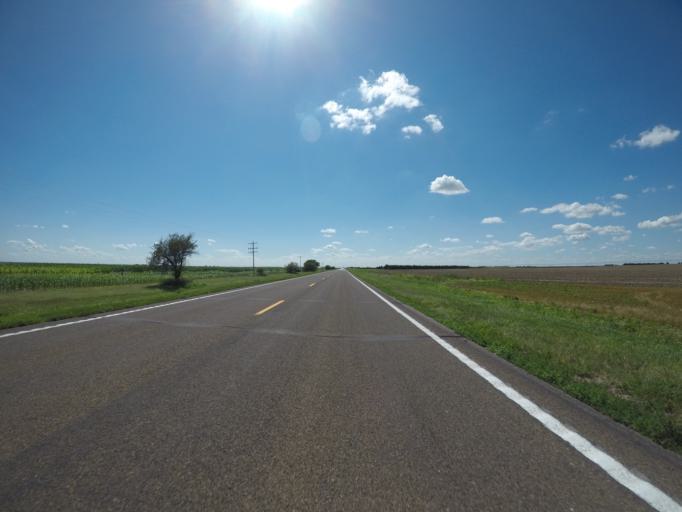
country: US
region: Nebraska
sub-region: Chase County
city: Imperial
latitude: 40.5377
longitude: -101.8784
